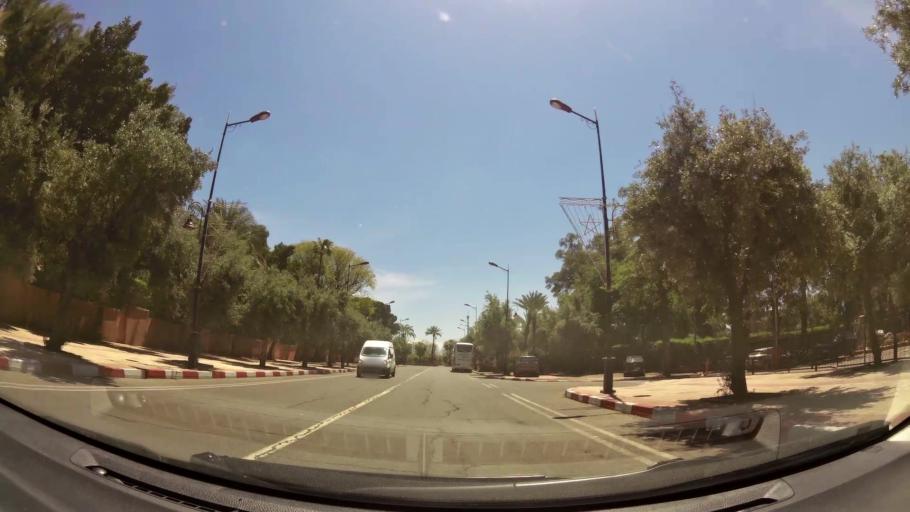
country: MA
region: Marrakech-Tensift-Al Haouz
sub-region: Marrakech
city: Marrakesh
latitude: 31.6207
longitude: -8.0065
